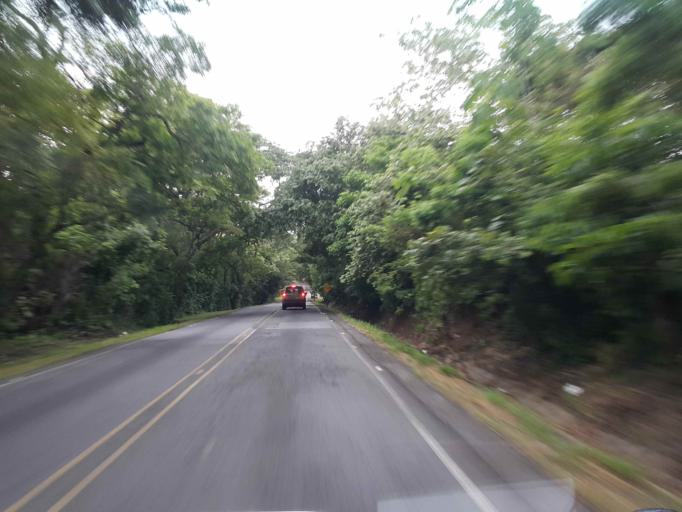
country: CR
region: Puntarenas
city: Miramar
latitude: 10.0779
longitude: -84.7803
